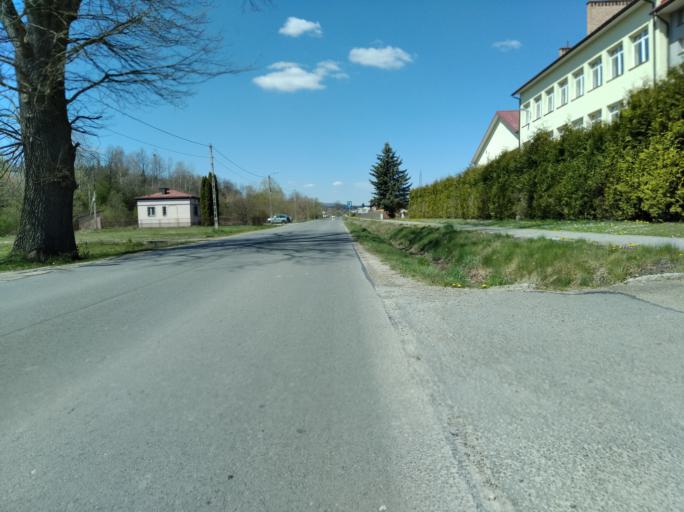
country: PL
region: Subcarpathian Voivodeship
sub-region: Powiat brzozowski
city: Dydnia
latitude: 49.6851
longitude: 22.1747
